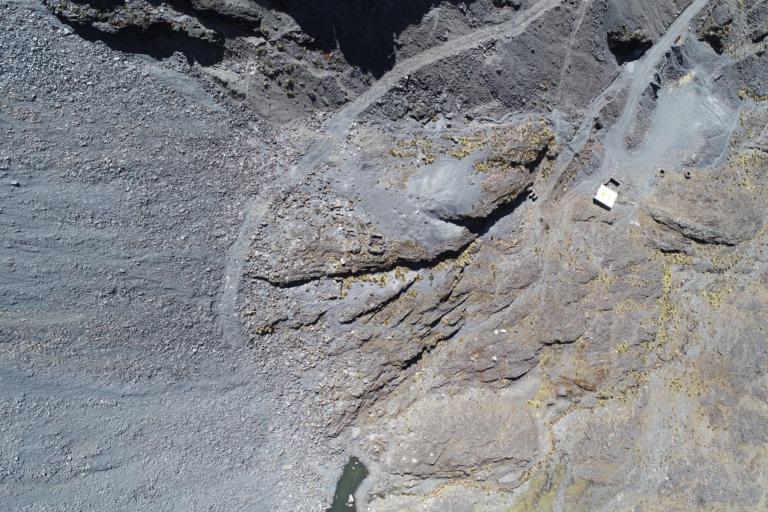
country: BO
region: La Paz
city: Sorata
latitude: -15.6704
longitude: -68.5637
